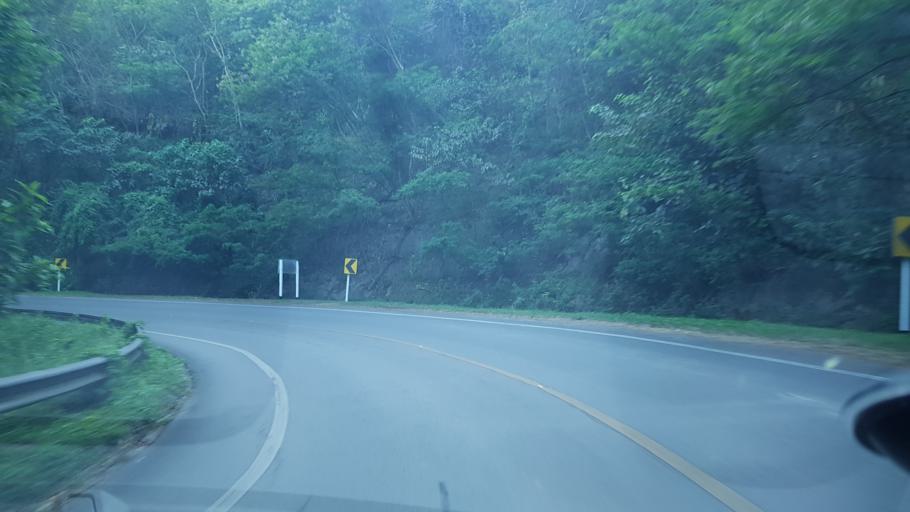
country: TH
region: Chiang Rai
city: Mae Fa Luang
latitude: 20.2959
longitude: 99.8152
